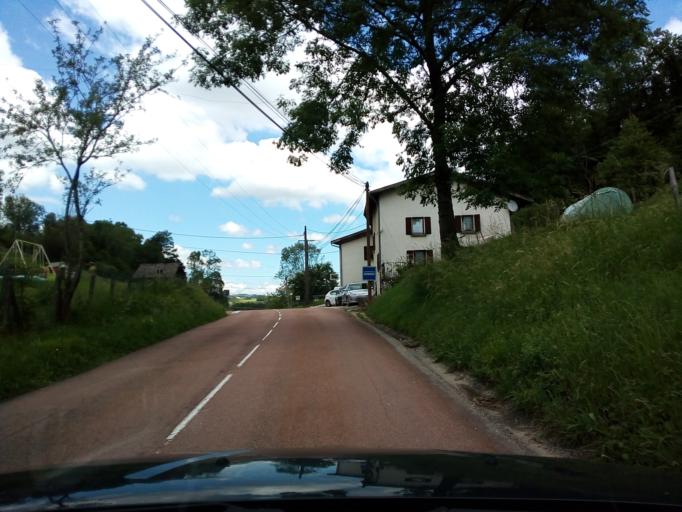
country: FR
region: Rhone-Alpes
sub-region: Departement de la Savoie
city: La Bridoire
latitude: 45.5296
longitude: 5.7625
